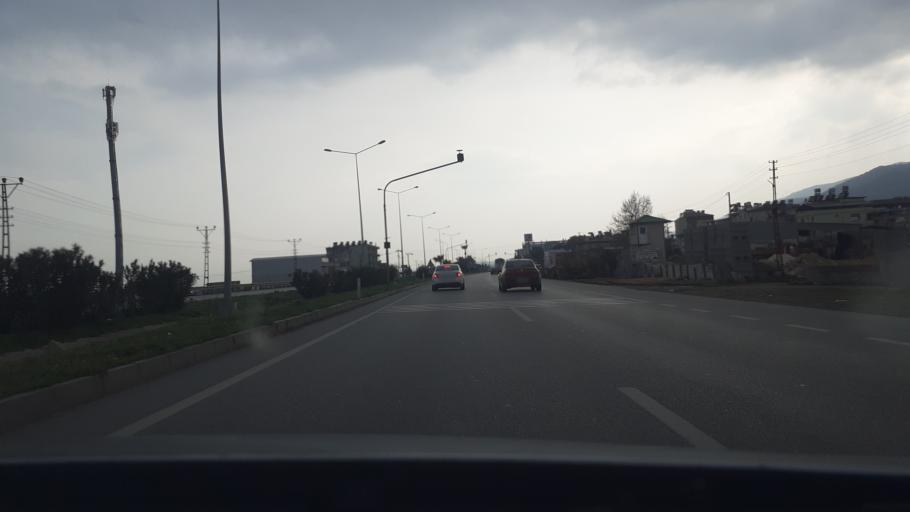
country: TR
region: Hatay
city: Serinyol
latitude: 36.3608
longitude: 36.2210
